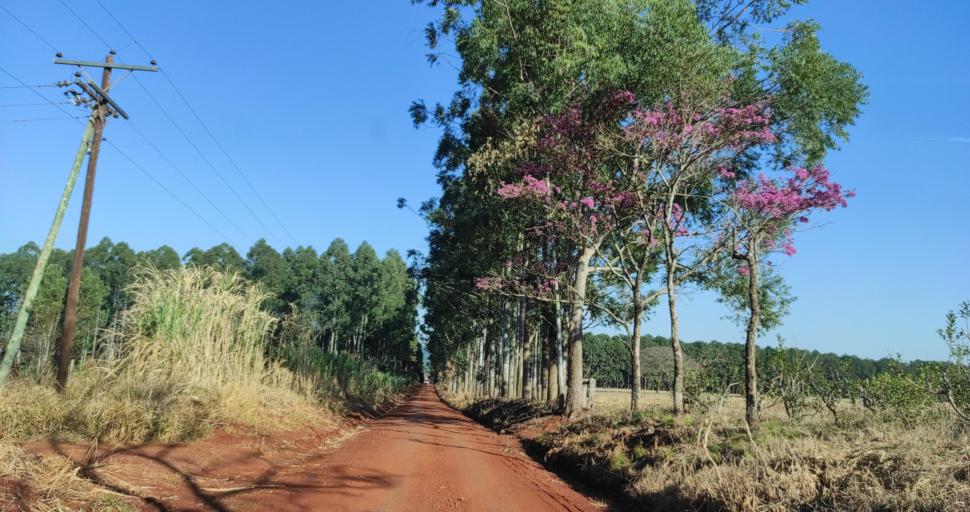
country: AR
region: Misiones
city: Puerto Rico
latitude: -26.8645
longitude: -55.0286
